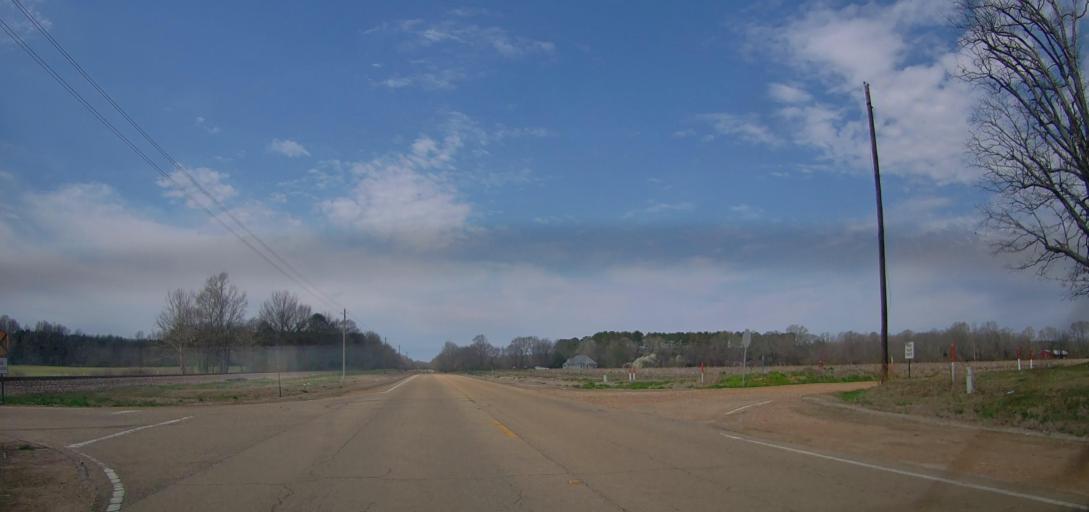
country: US
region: Mississippi
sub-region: Benton County
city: Ashland
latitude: 34.6229
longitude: -89.2411
